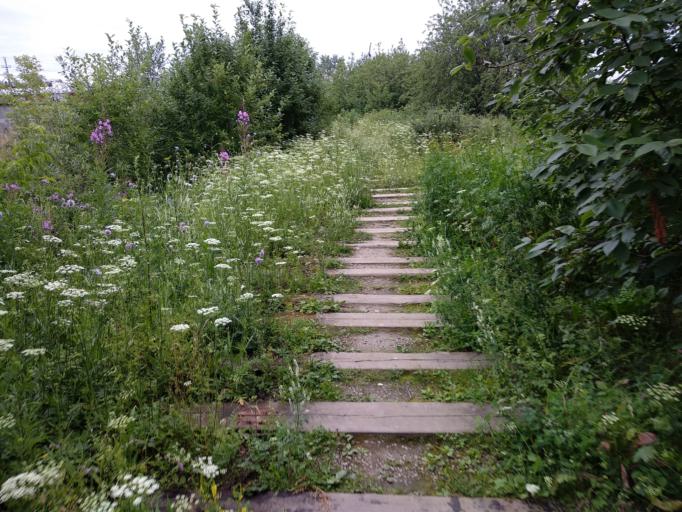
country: RU
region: Sverdlovsk
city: Beryozovsky
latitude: 56.9221
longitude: 60.7784
